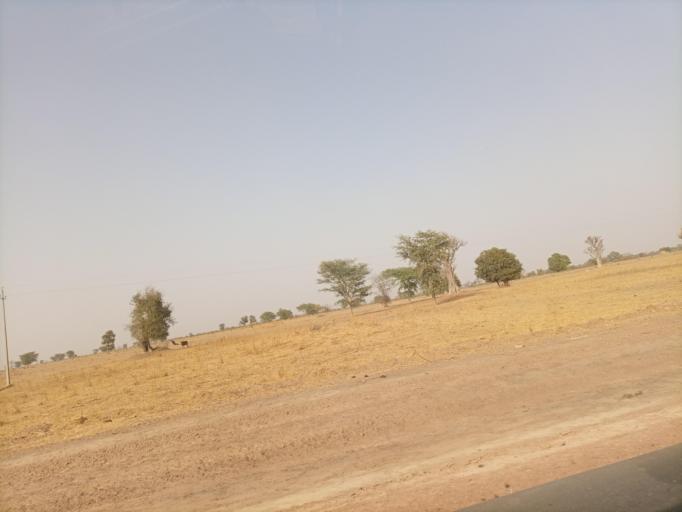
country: SN
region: Fatick
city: Passi
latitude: 14.0279
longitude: -16.3063
